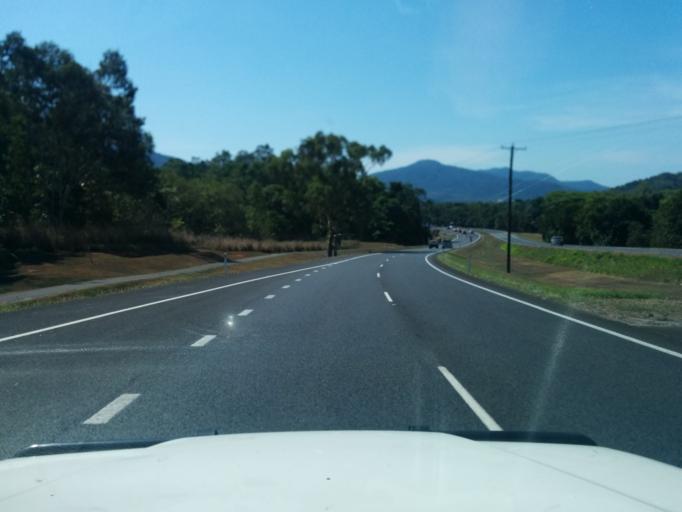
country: AU
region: Queensland
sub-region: Cairns
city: Redlynch
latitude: -16.9089
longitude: 145.7125
